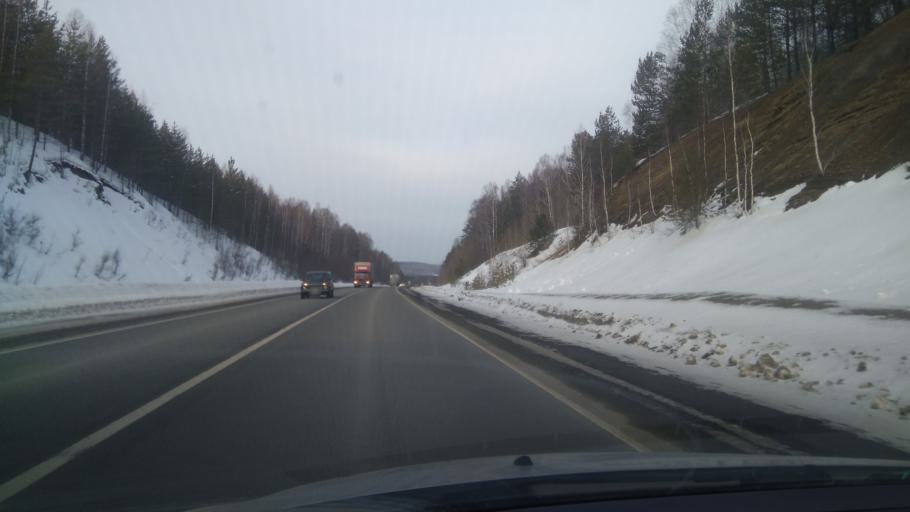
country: RU
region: Sverdlovsk
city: Bisert'
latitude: 56.8349
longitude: 58.8883
